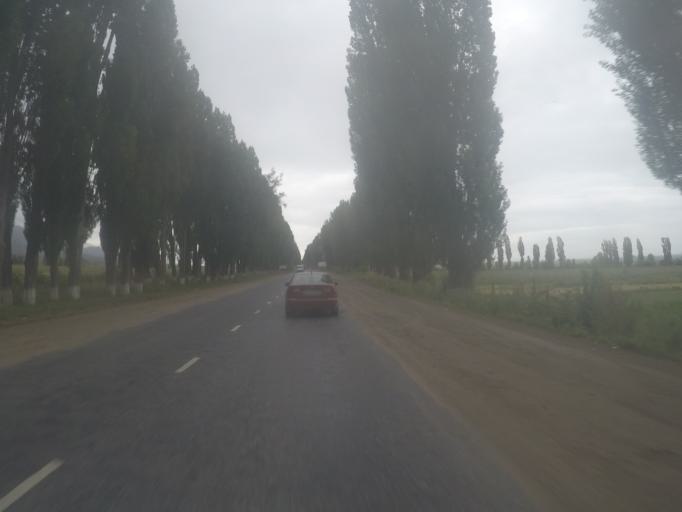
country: KG
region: Ysyk-Koel
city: Cholpon-Ata
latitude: 42.6922
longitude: 77.3753
